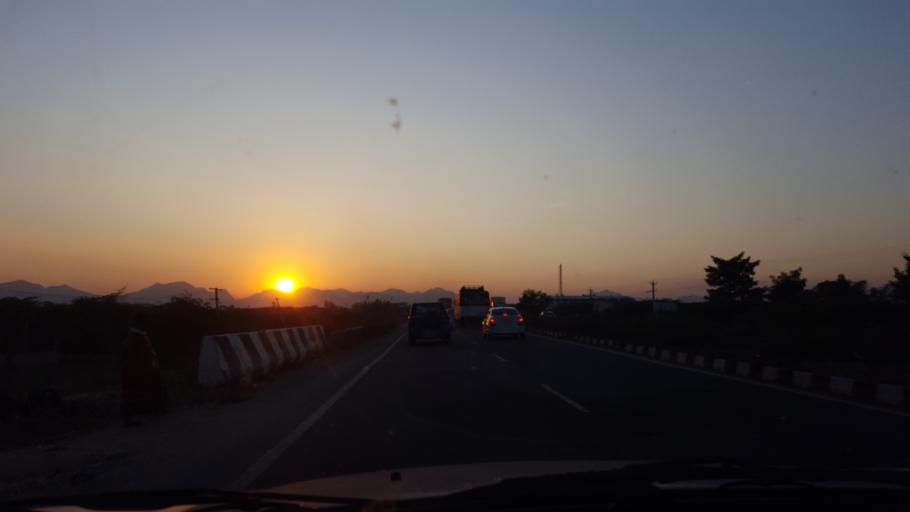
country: IN
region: Andhra Pradesh
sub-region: Chittoor
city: Tirupati
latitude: 13.6043
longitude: 79.3887
